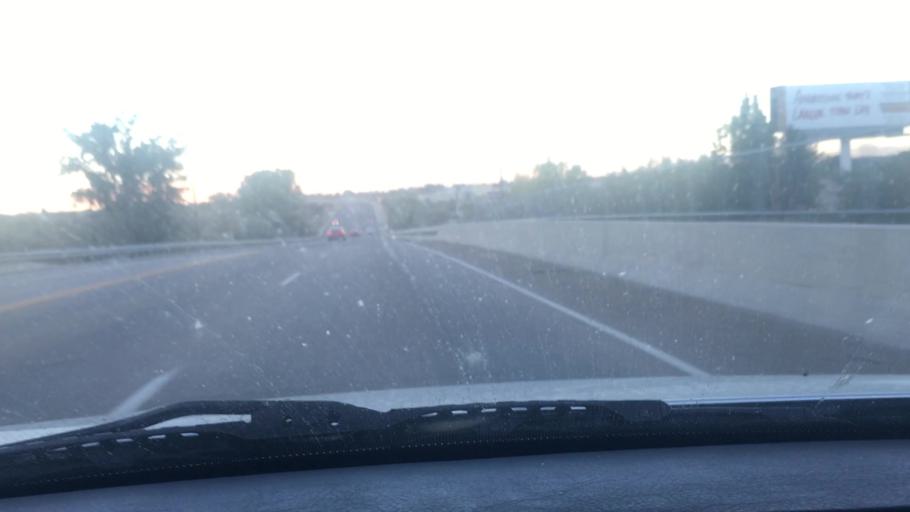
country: US
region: Utah
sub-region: Utah County
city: Provo
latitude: 40.2079
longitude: -111.6334
